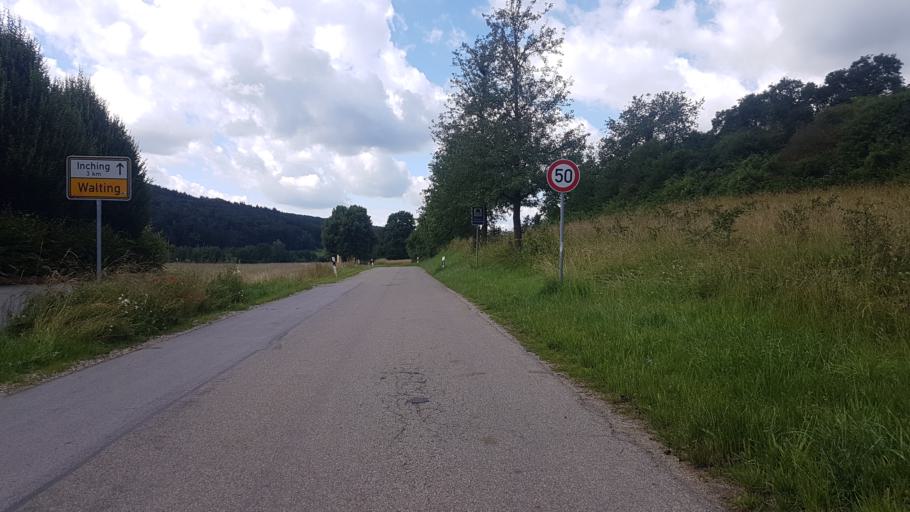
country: DE
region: Bavaria
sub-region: Upper Bavaria
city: Walting
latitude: 48.9108
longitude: 11.2998
